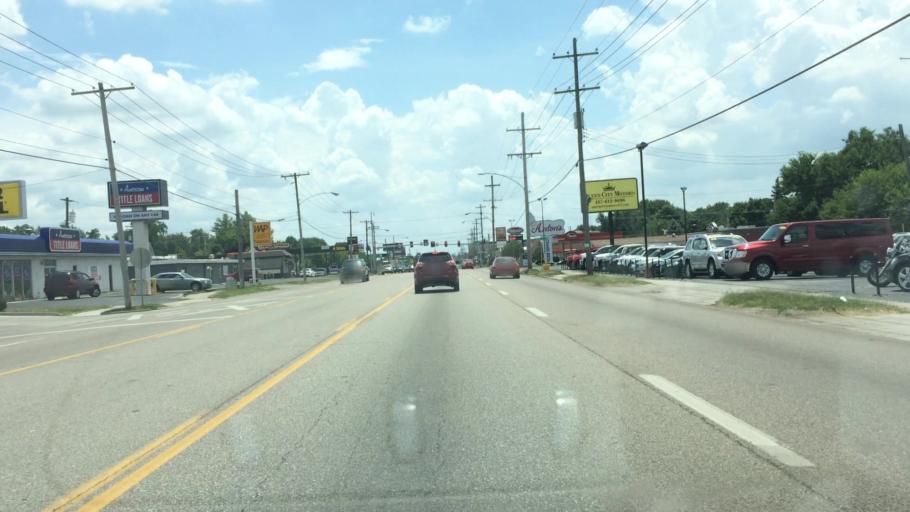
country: US
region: Missouri
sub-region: Greene County
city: Springfield
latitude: 37.1981
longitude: -93.2621
